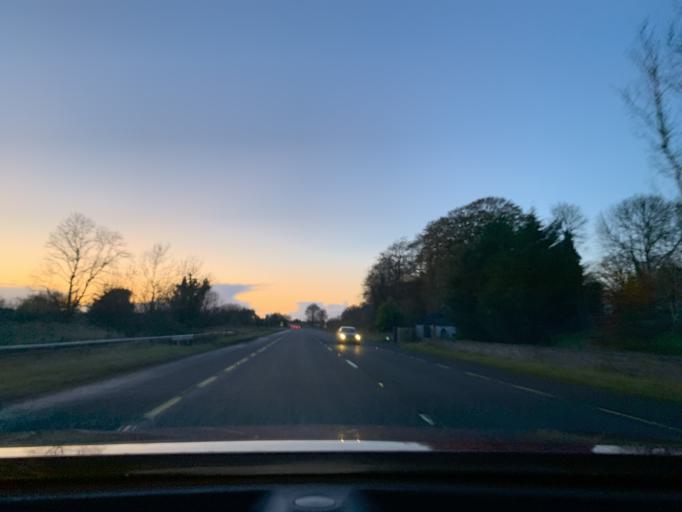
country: IE
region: Connaught
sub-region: County Leitrim
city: Carrick-on-Shannon
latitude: 53.9580
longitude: -8.1697
